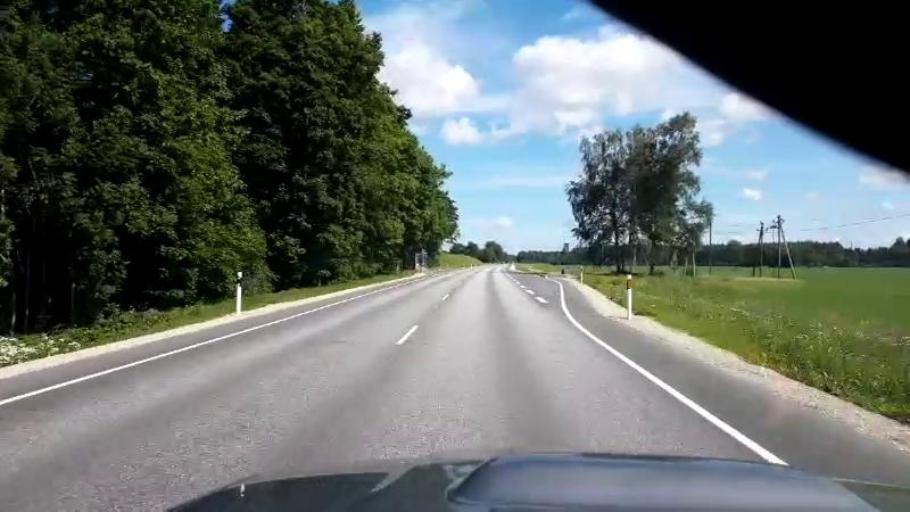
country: EE
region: Jaervamaa
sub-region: Paide linn
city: Paide
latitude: 58.9851
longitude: 25.6693
